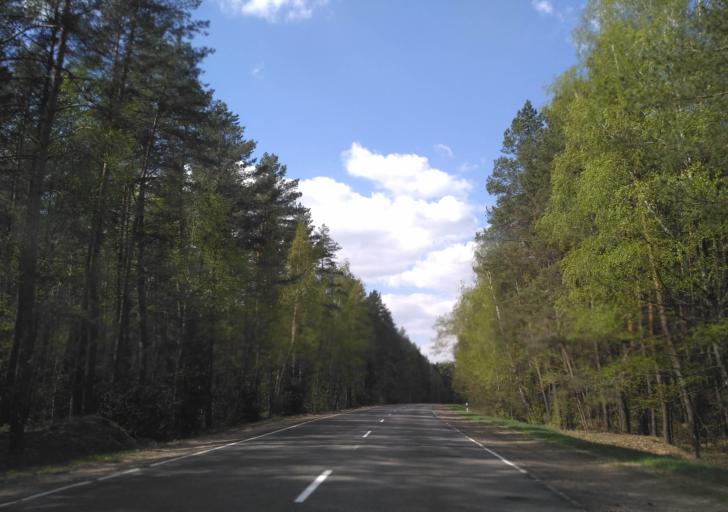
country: BY
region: Minsk
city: Vilyeyka
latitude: 54.4990
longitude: 27.0907
